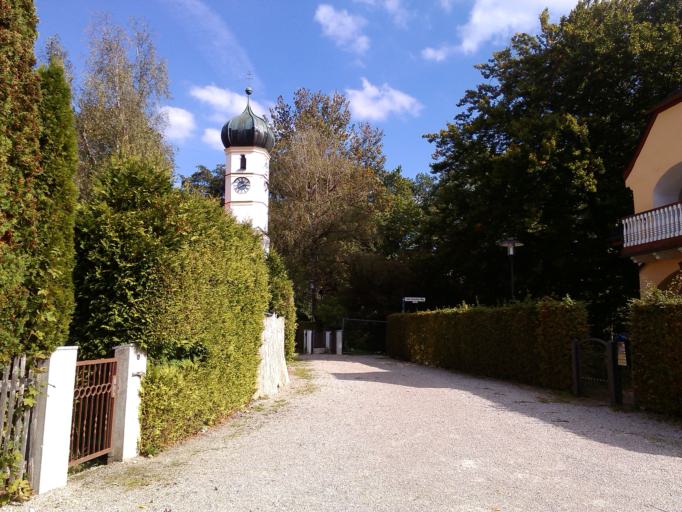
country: DE
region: Bavaria
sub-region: Upper Bavaria
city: Planegg
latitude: 48.0990
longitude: 11.4180
